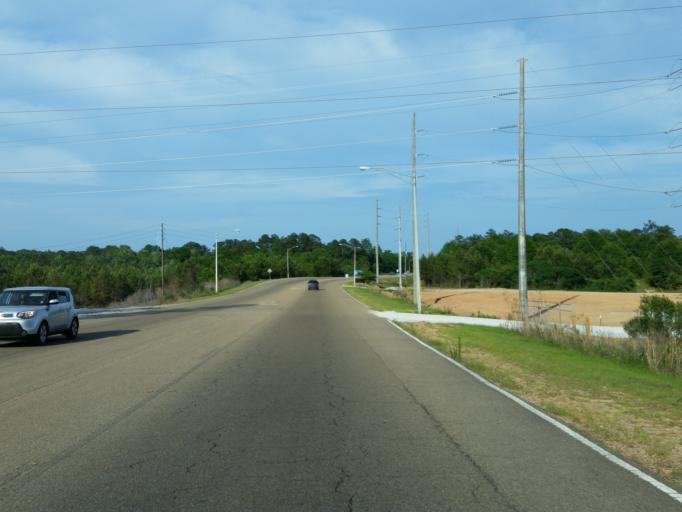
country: US
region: Mississippi
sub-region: Lamar County
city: West Hattiesburg
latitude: 31.3038
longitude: -89.3564
